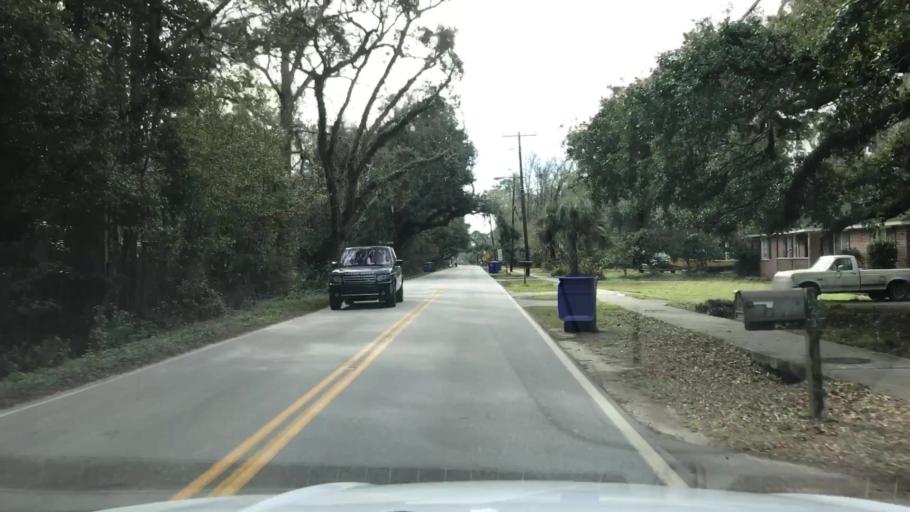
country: US
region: South Carolina
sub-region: Charleston County
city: North Charleston
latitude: 32.7811
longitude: -80.0198
